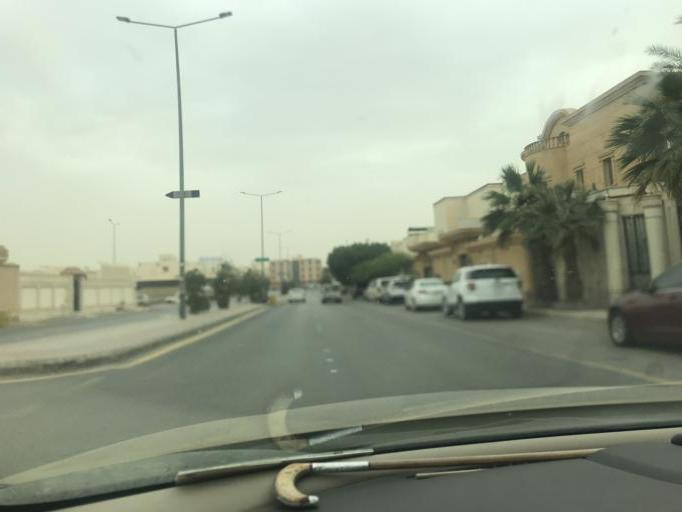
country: SA
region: Ar Riyad
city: Riyadh
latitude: 24.7391
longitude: 46.7538
